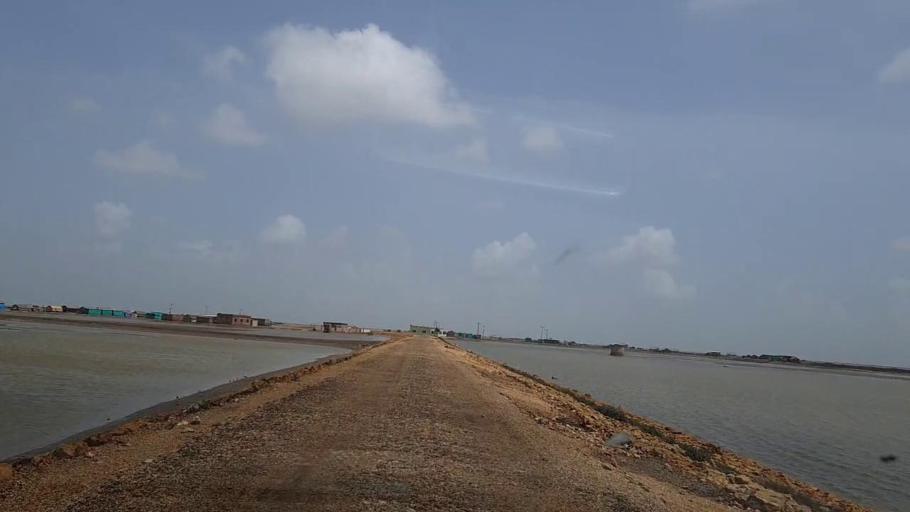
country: PK
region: Sindh
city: Keti Bandar
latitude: 24.1307
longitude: 67.4659
